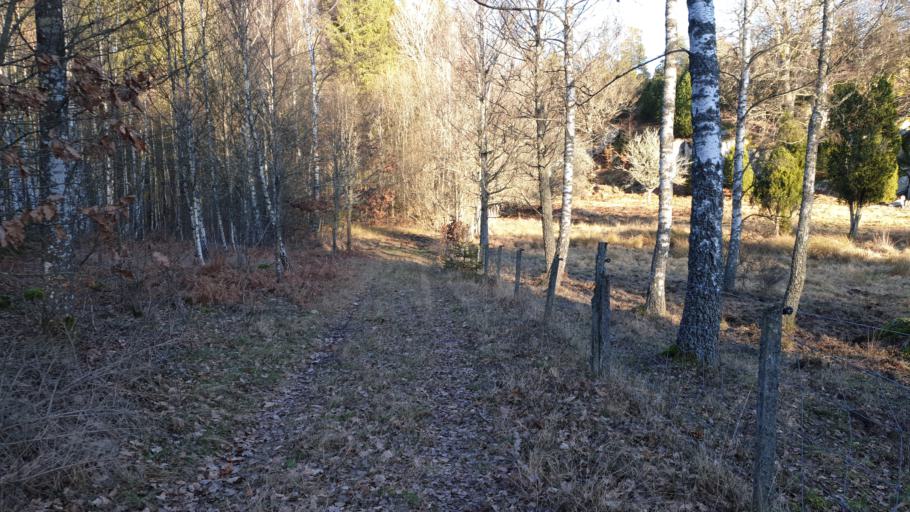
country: SE
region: Blekinge
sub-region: Ronneby Kommun
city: Brakne-Hoby
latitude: 56.2321
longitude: 15.1809
